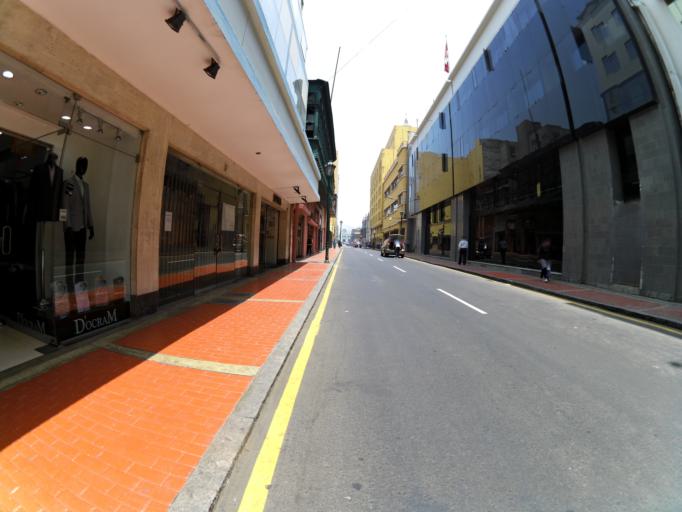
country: PE
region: Lima
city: Lima
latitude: -12.0475
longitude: -77.0310
